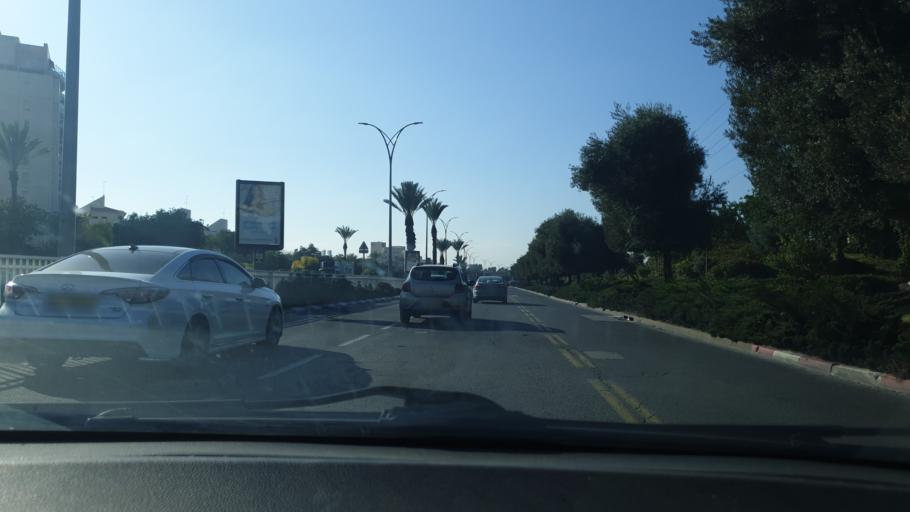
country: IL
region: Central District
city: Rishon LeZiyyon
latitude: 31.9800
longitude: 34.7782
